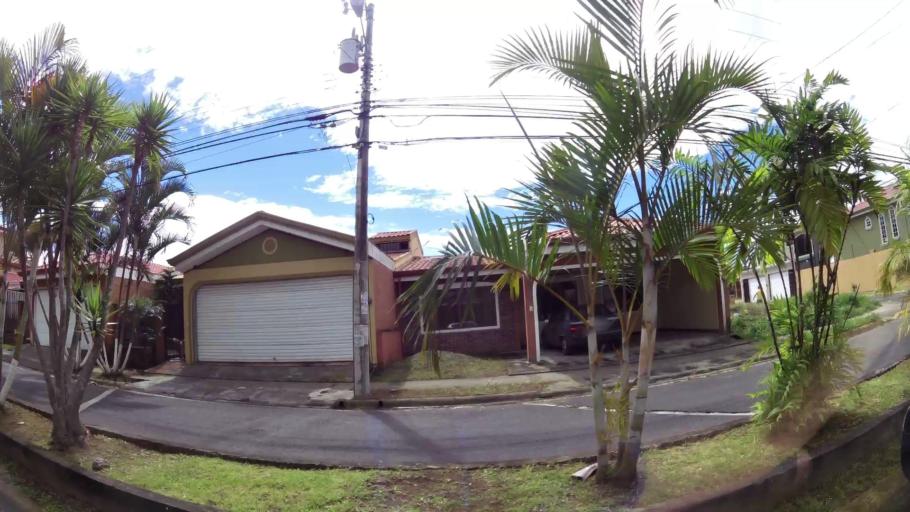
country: CR
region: Cartago
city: Concepcion
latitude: 9.9230
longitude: -83.9996
